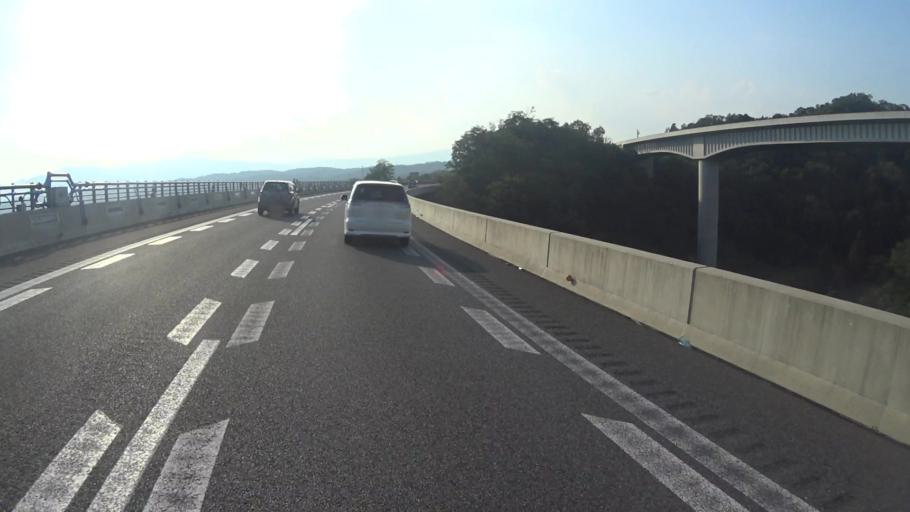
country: JP
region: Shiga Prefecture
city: Kusatsu
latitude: 34.9577
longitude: 135.9740
